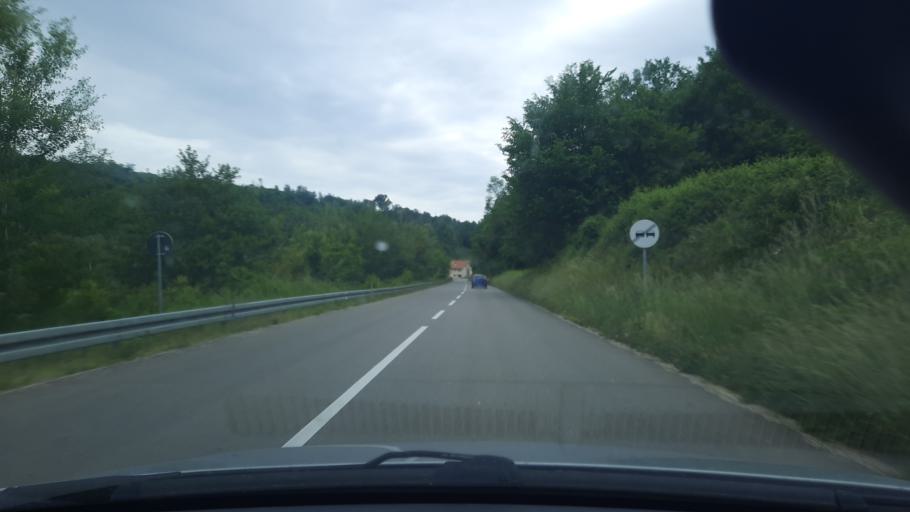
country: RS
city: Bukor
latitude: 44.5036
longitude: 19.4956
